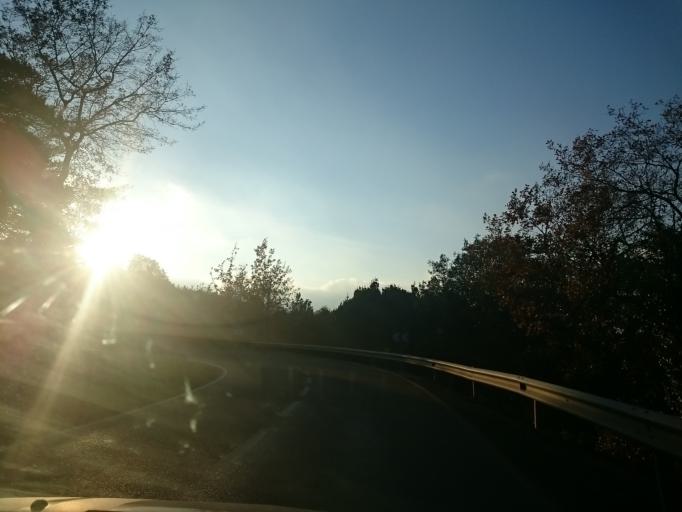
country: ES
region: Catalonia
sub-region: Provincia de Barcelona
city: Seva
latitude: 41.8420
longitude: 2.3124
